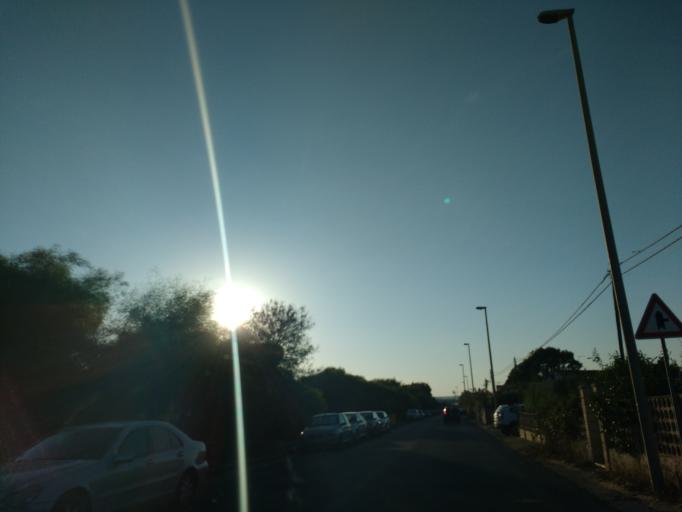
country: IT
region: Sicily
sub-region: Ragusa
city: Ispica
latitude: 36.7221
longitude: 14.9168
